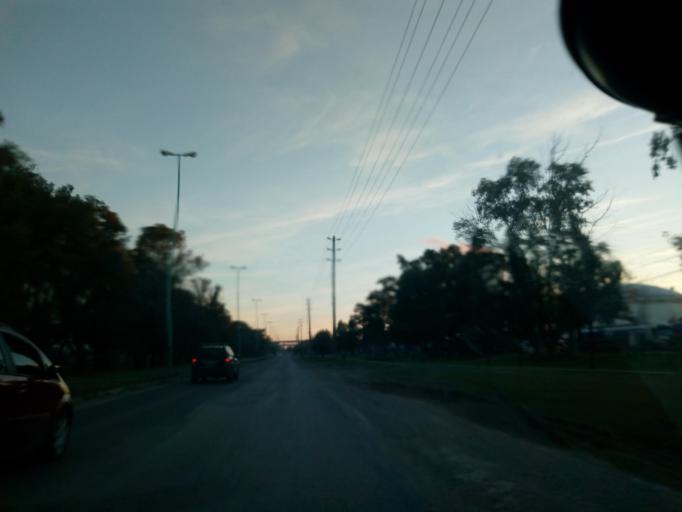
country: AR
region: Buenos Aires
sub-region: Partido de Ensenada
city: Ensenada
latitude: -34.8763
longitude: -57.9183
